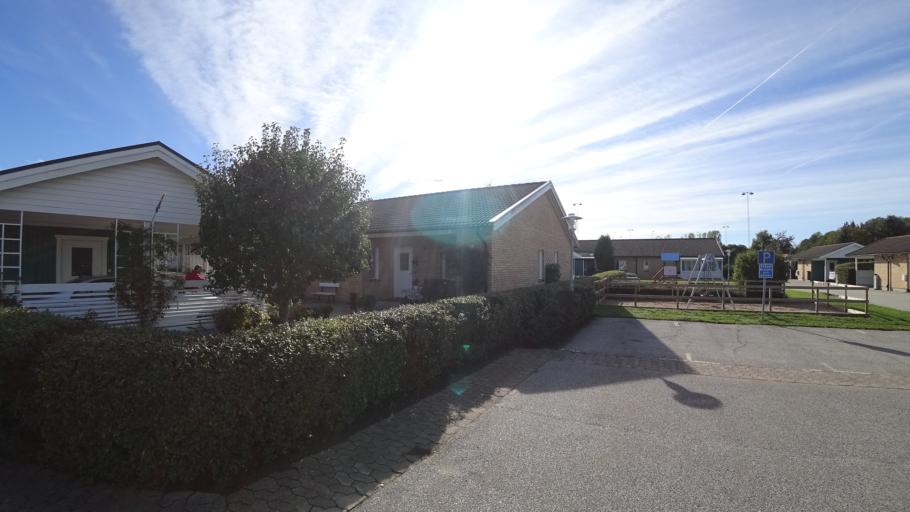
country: SE
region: Skane
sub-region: Kavlinge Kommun
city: Kaevlinge
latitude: 55.8008
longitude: 13.1085
